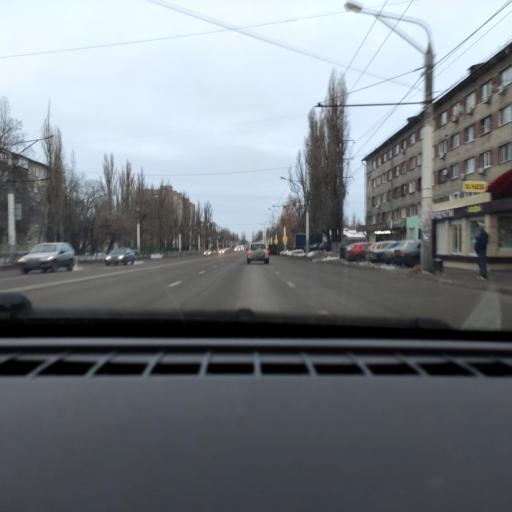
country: RU
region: Voronezj
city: Maslovka
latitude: 51.6096
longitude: 39.2361
